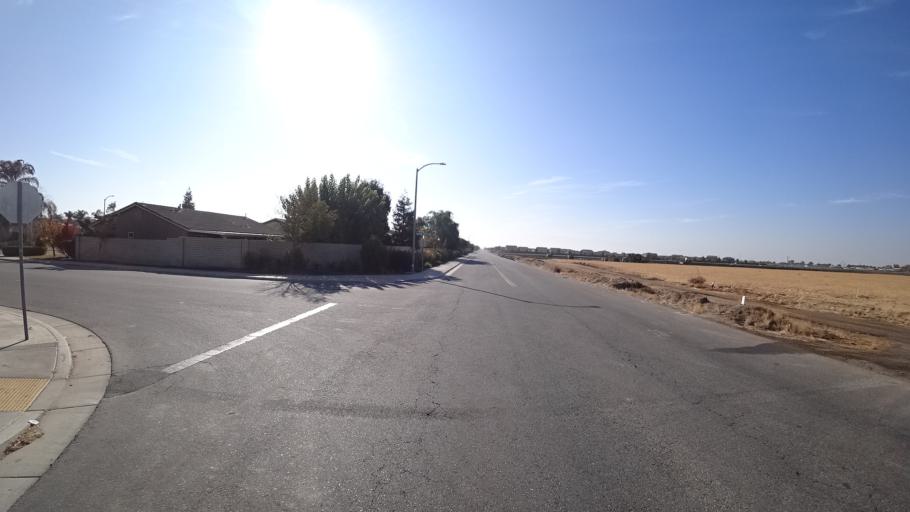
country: US
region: California
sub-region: Kern County
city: Greenfield
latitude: 35.2849
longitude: -119.0655
